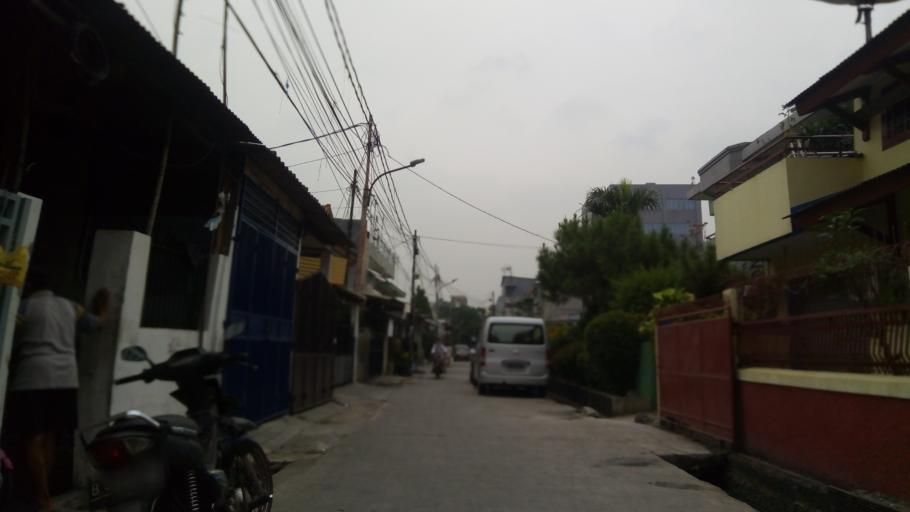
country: ID
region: Jakarta Raya
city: Jakarta
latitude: -6.1524
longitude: 106.8373
